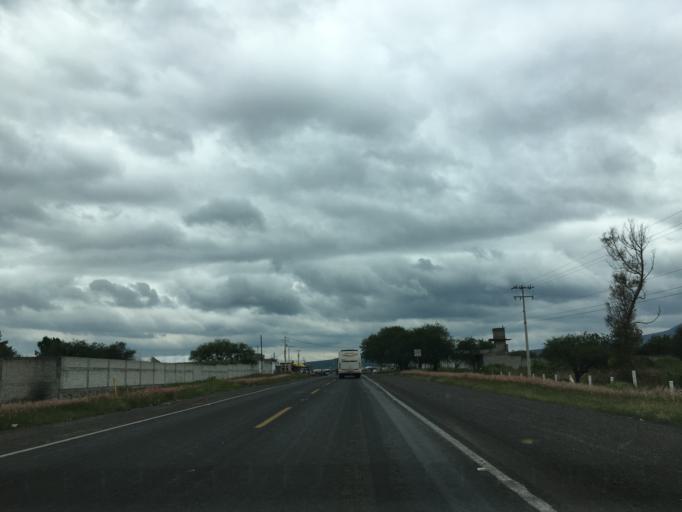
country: MX
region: Michoacan
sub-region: Cuitzeo
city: Cuamio
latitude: 20.0536
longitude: -101.1504
